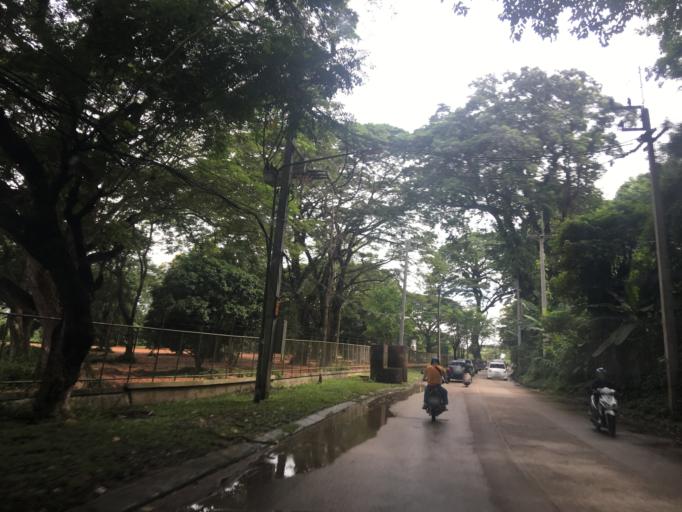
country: TH
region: Chiang Rai
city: Chiang Rai
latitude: 19.9151
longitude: 99.8218
